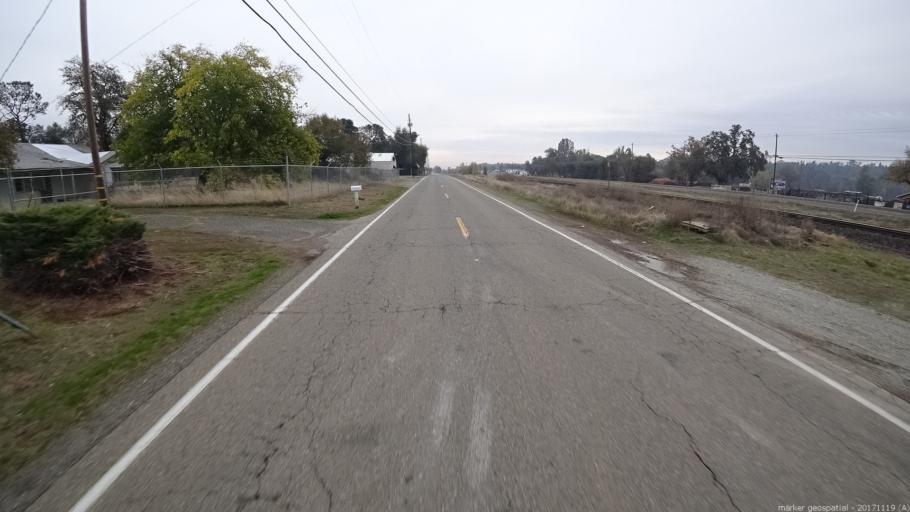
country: US
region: California
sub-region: Shasta County
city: Anderson
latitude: 40.4918
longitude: -122.3610
